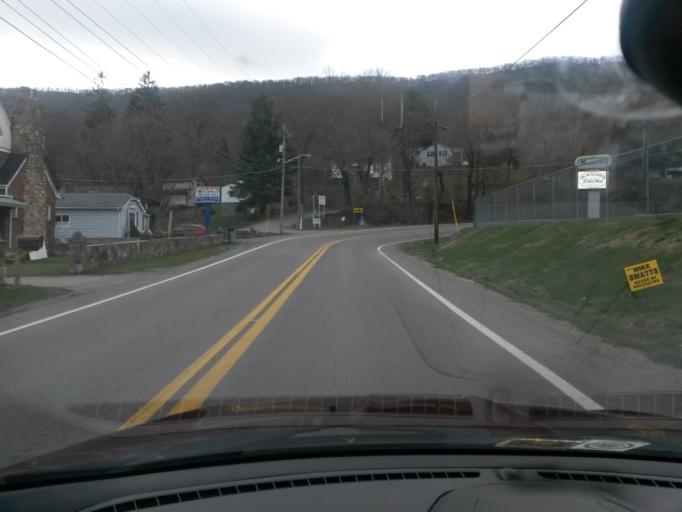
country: US
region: West Virginia
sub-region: Mercer County
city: Bluefield
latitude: 37.2500
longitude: -81.2130
